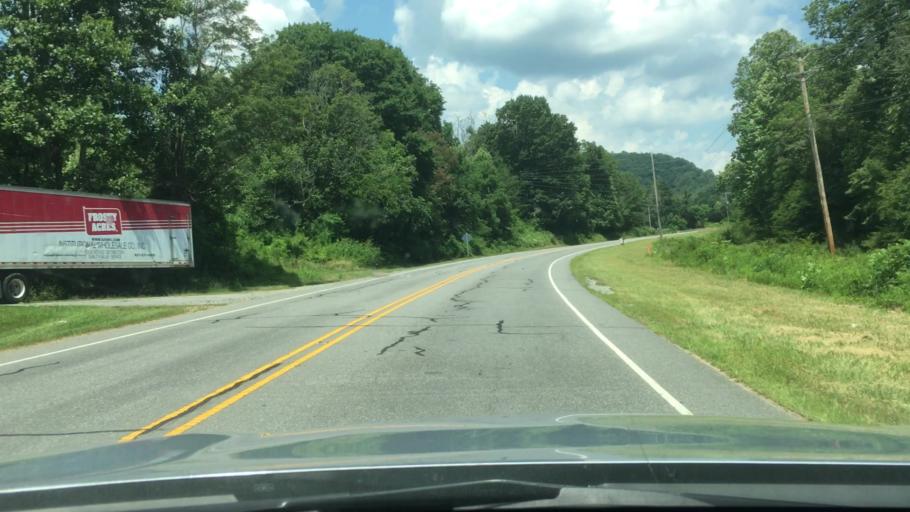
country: US
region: North Carolina
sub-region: Madison County
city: Marshall
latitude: 35.8180
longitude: -82.6511
